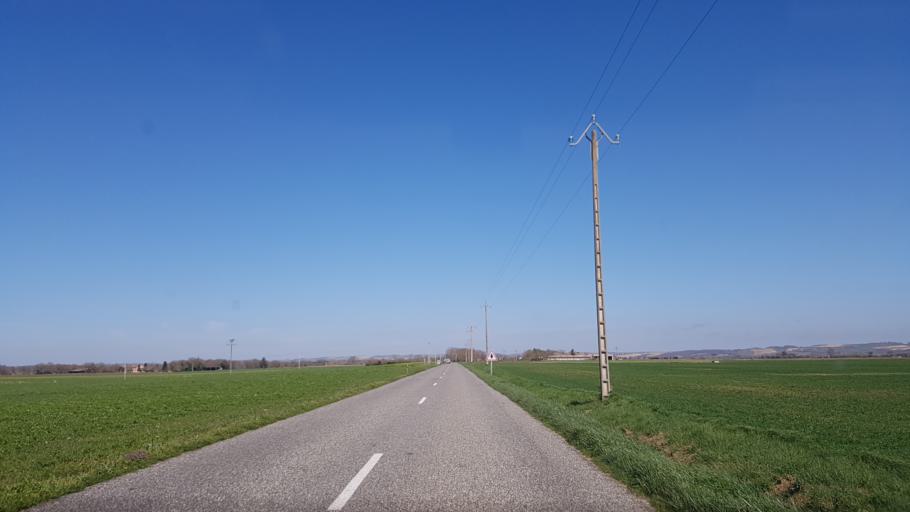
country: FR
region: Languedoc-Roussillon
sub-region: Departement de l'Aude
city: Belpech
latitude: 43.1703
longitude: 1.7099
